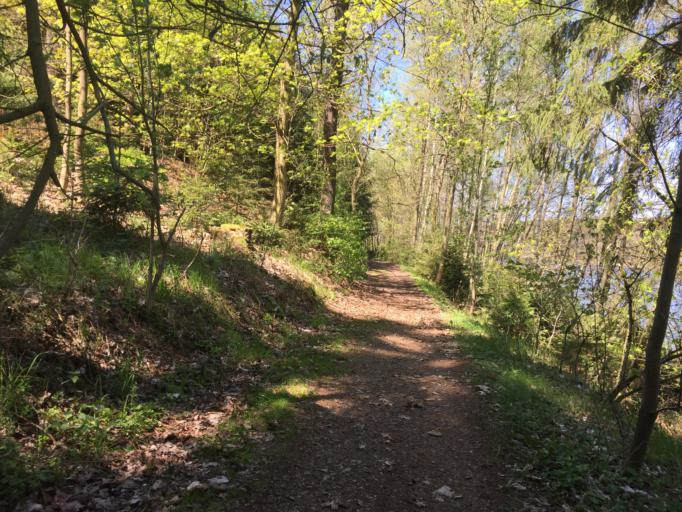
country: DE
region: Saxony
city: Neuensalz
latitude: 50.5254
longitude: 12.2053
